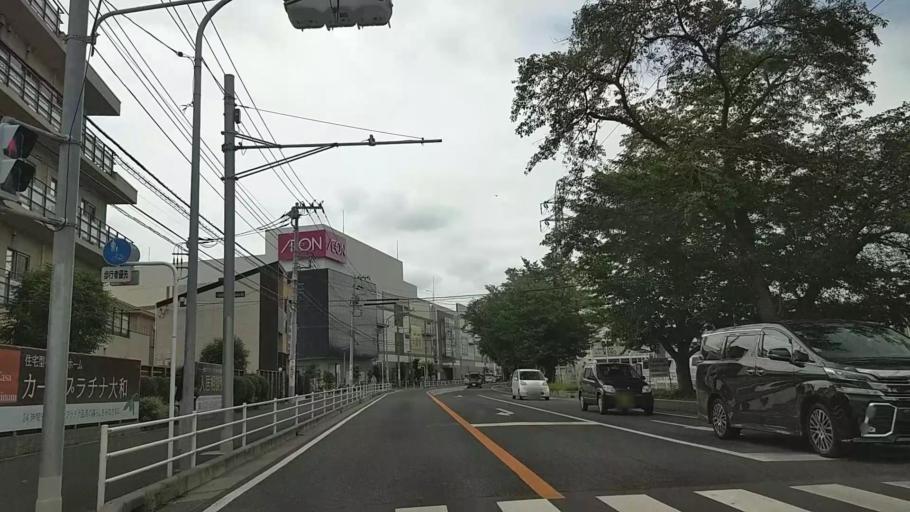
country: JP
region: Kanagawa
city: Minami-rinkan
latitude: 35.4334
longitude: 139.4671
